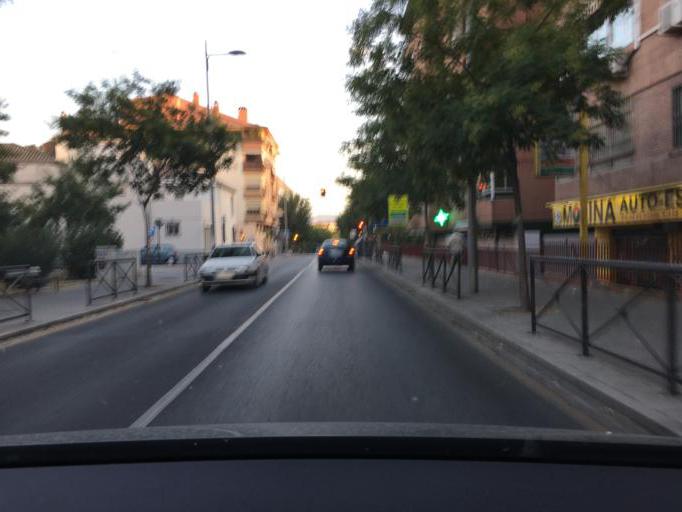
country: ES
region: Andalusia
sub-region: Provincia de Granada
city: Granada
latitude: 37.1906
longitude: -3.6038
